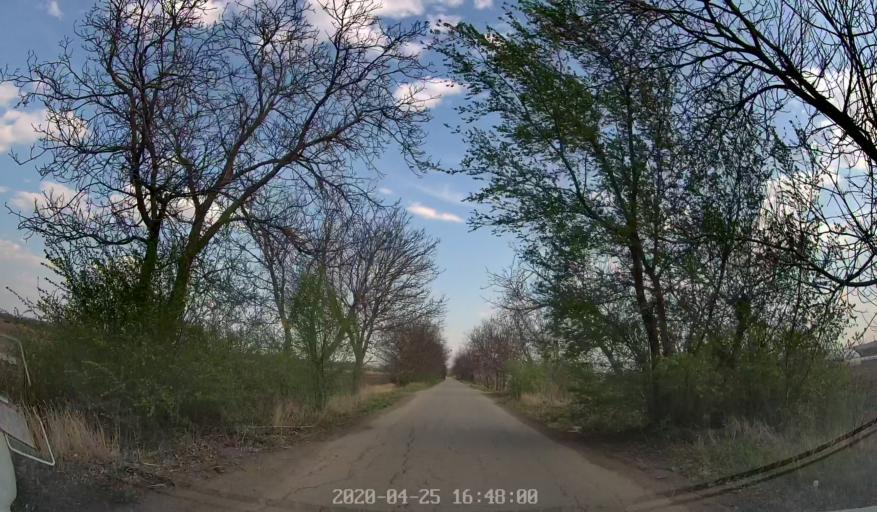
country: MD
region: Chisinau
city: Vadul lui Voda
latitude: 47.1335
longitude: 29.0770
